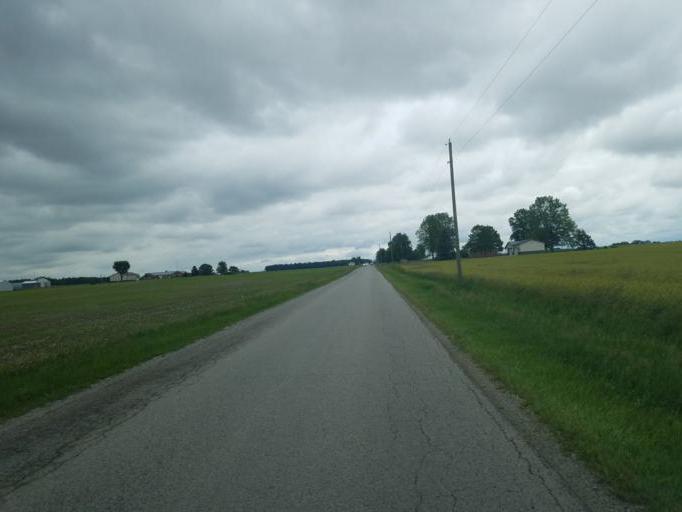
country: US
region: Ohio
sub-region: Crawford County
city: Bucyrus
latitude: 40.7757
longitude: -82.9737
